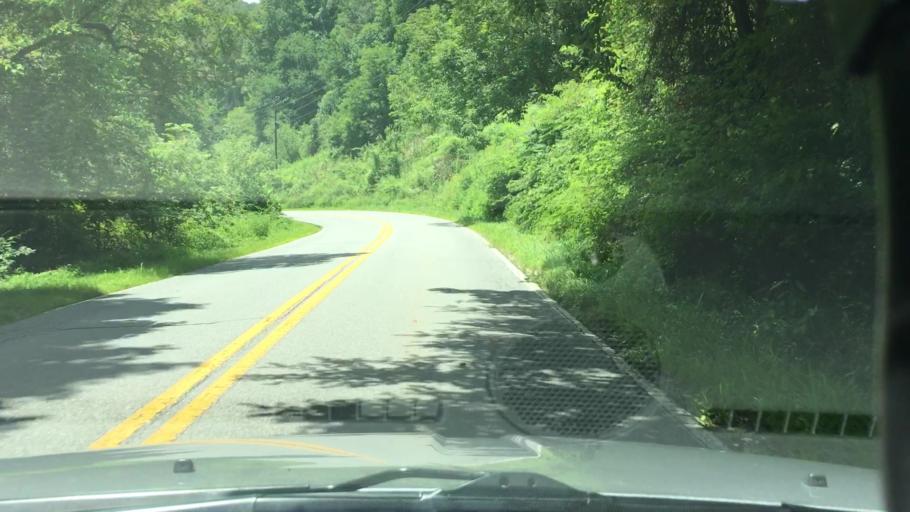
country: US
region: North Carolina
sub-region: Madison County
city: Mars Hill
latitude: 35.9197
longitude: -82.5321
